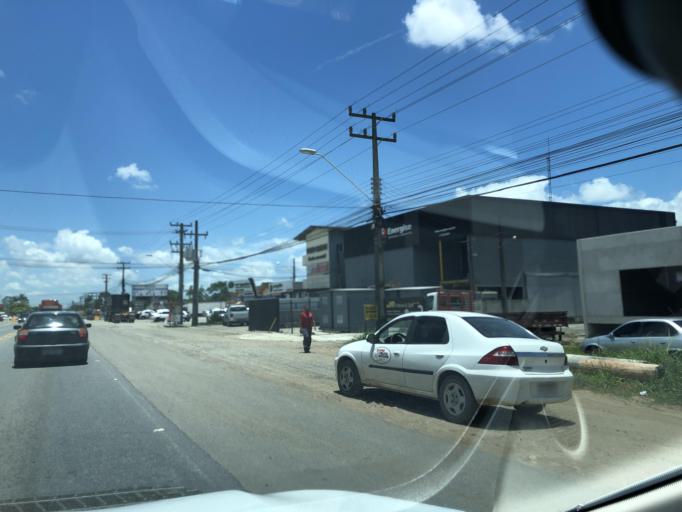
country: BR
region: Santa Catarina
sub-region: Joinville
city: Joinville
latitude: -26.4064
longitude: -48.7476
